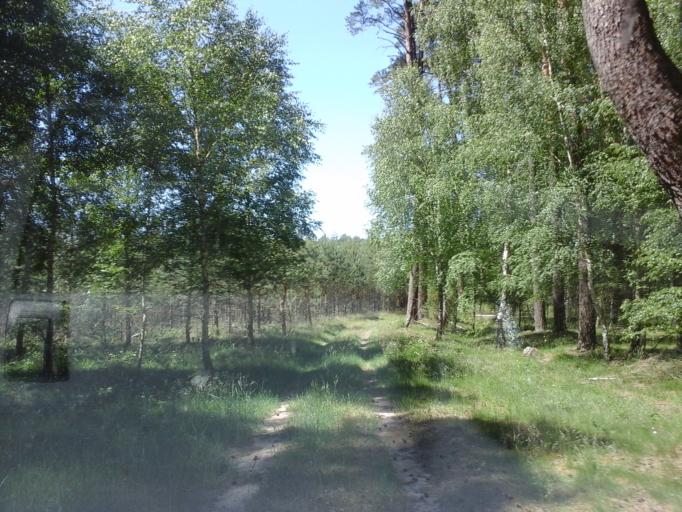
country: PL
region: West Pomeranian Voivodeship
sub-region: Powiat walecki
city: Miroslawiec
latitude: 53.2321
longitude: 16.0370
